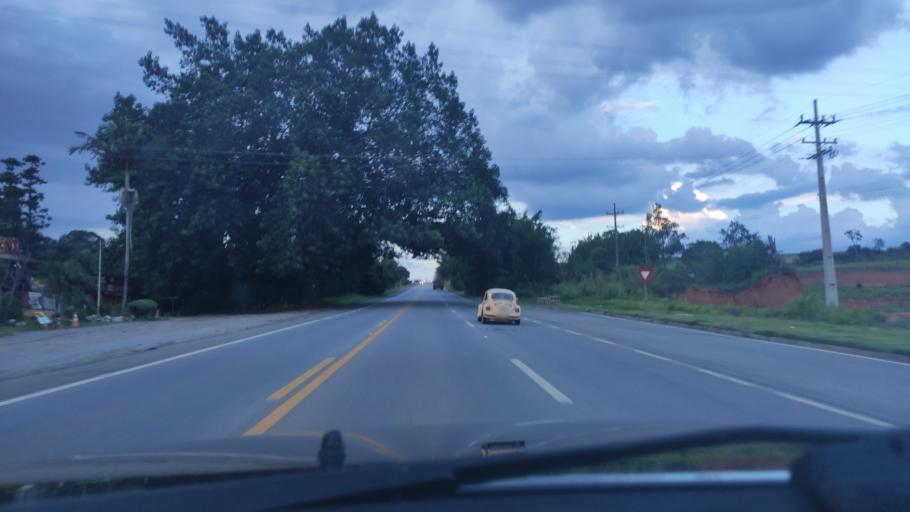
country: BR
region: Sao Paulo
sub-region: Braganca Paulista
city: Braganca Paulista
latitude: -22.8905
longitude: -46.5412
